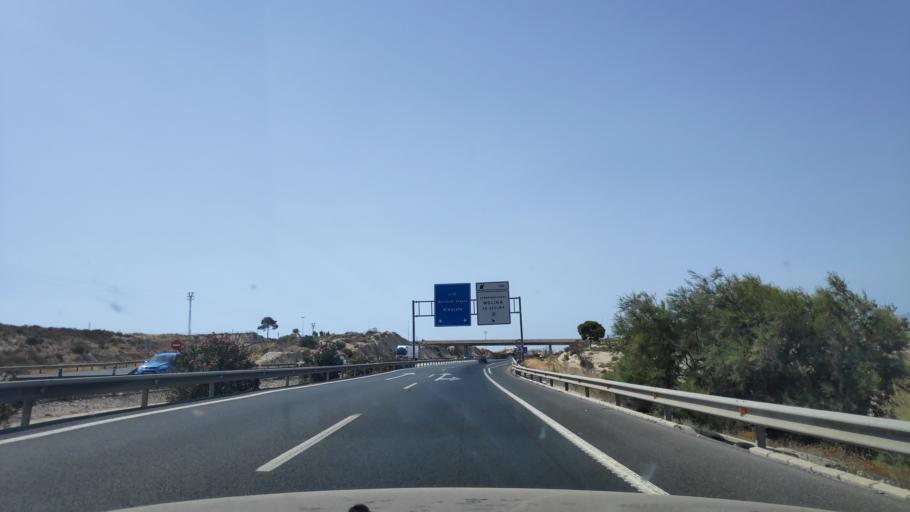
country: ES
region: Murcia
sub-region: Murcia
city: Molina de Segura
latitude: 38.0586
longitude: -1.1887
